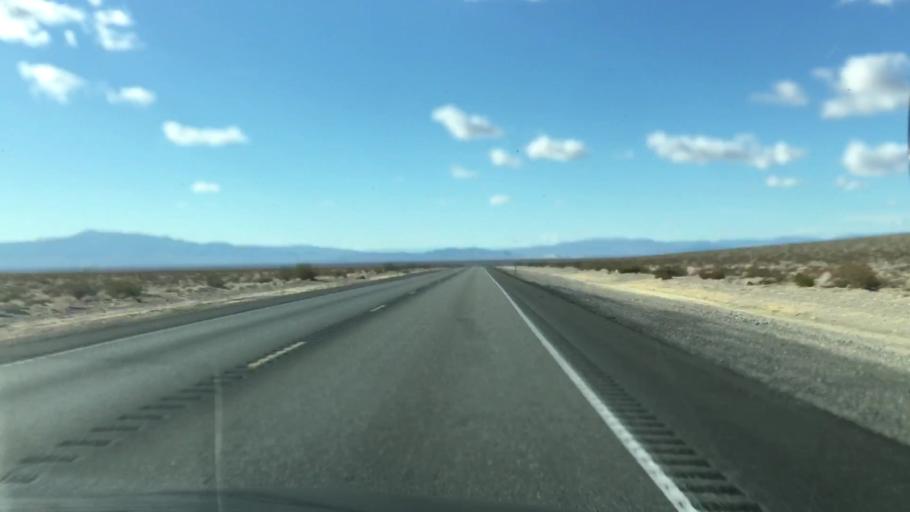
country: US
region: Nevada
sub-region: Nye County
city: Beatty
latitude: 36.6317
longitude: -116.3348
